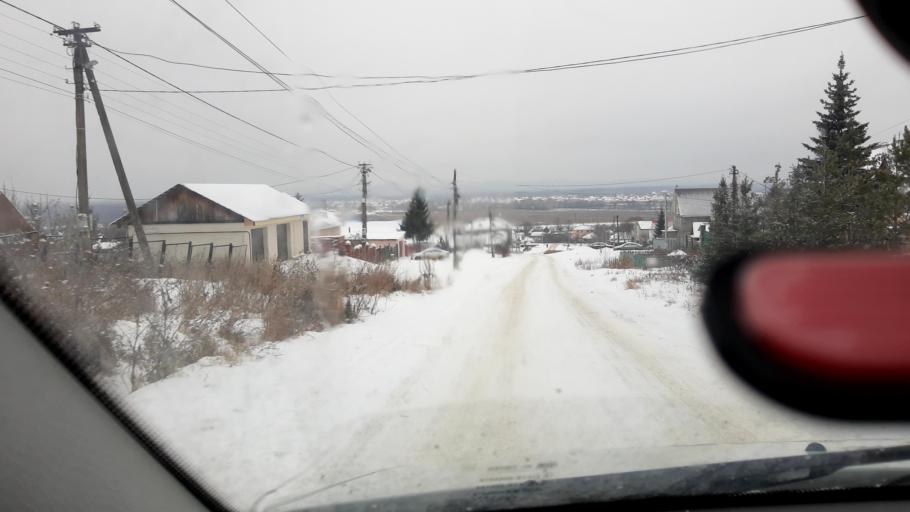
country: RU
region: Bashkortostan
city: Kabakovo
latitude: 54.6349
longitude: 56.0835
